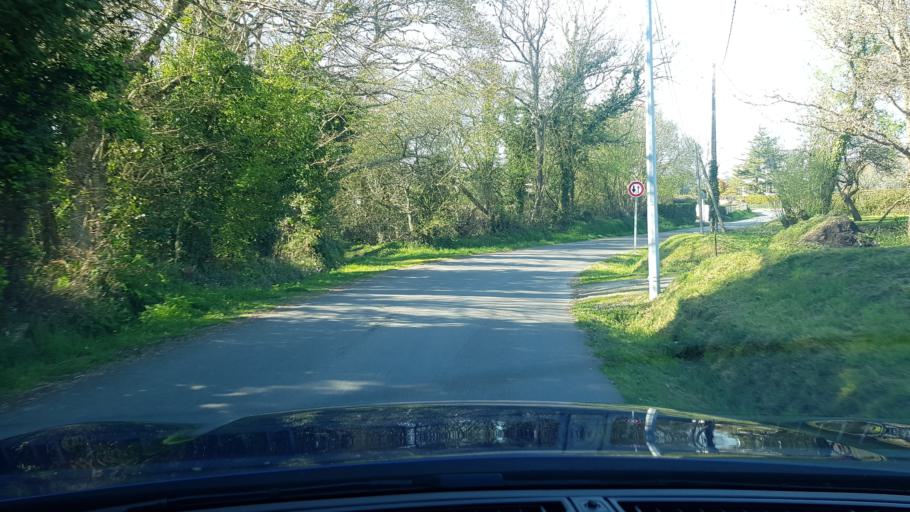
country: FR
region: Brittany
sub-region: Departement du Finistere
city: Clohars-Carnoet
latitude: 47.7782
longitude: -3.6172
